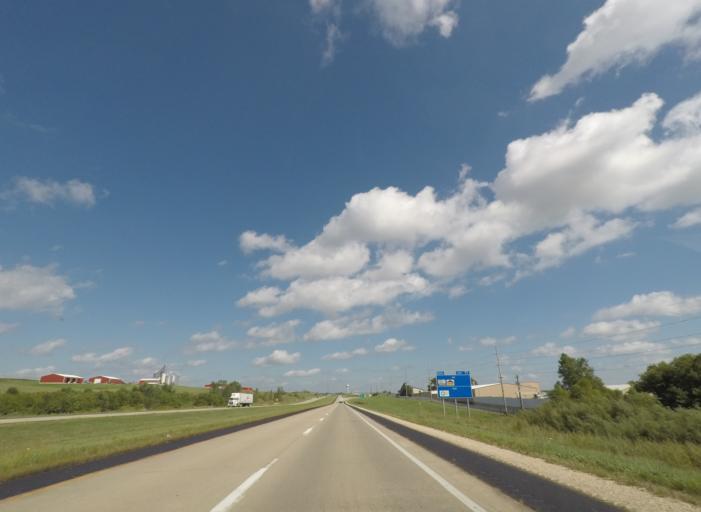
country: US
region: Iowa
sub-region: Dubuque County
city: Cascade
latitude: 42.3107
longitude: -91.0091
